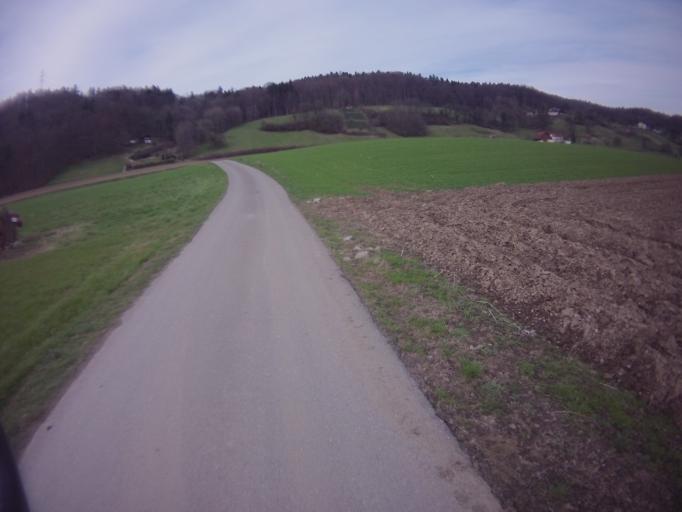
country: CH
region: Aargau
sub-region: Bezirk Baden
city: Wurenlos
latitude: 47.4303
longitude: 8.3848
